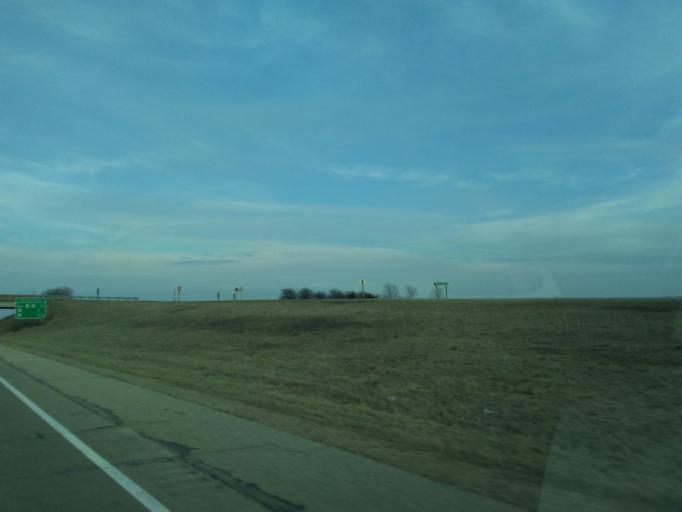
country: US
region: Wisconsin
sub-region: Dane County
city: Verona
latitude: 42.9873
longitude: -89.5844
